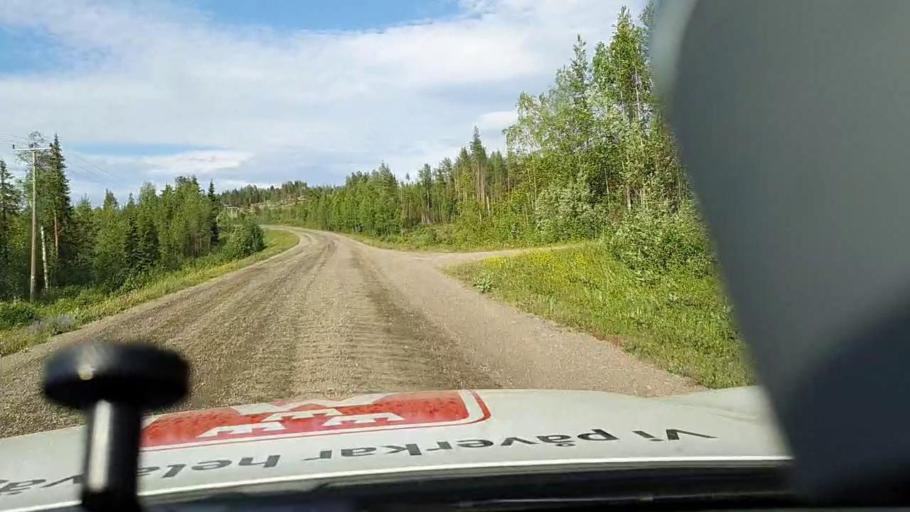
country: SE
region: Norrbotten
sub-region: Alvsbyns Kommun
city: AElvsbyn
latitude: 66.1642
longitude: 21.0541
